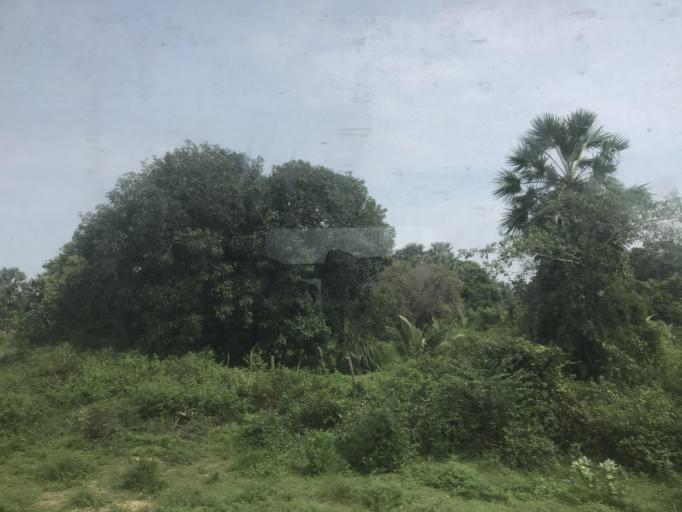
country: LK
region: Northern Province
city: Kilinochchi
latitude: 9.5870
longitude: 80.3491
